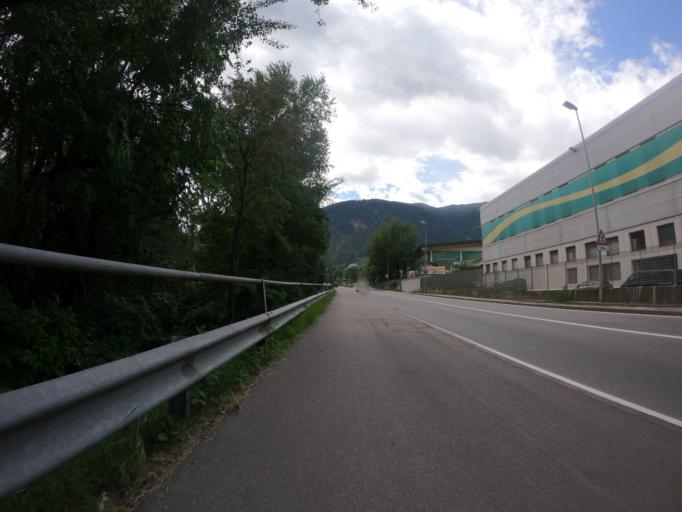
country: IT
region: Trentino-Alto Adige
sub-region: Bolzano
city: Sinigo
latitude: 46.6284
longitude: 11.1685
